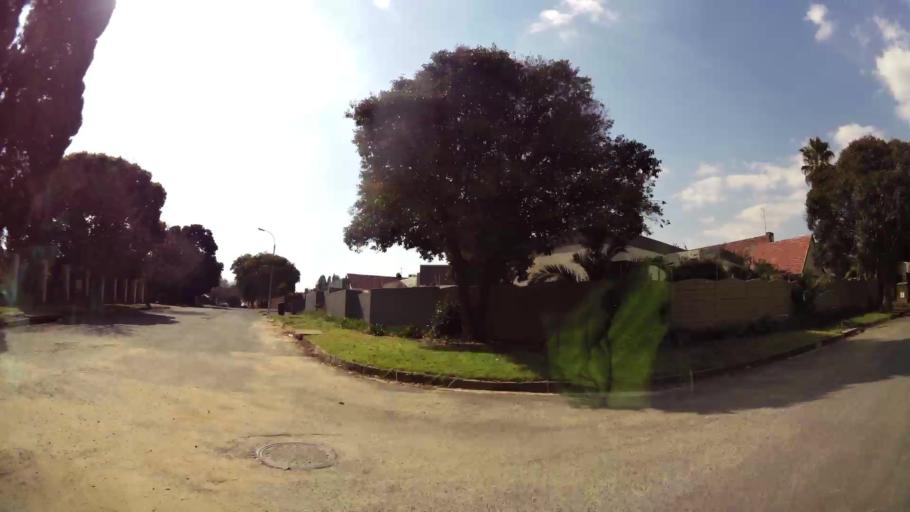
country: ZA
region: Gauteng
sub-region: City of Johannesburg Metropolitan Municipality
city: Modderfontein
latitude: -26.0863
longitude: 28.2268
